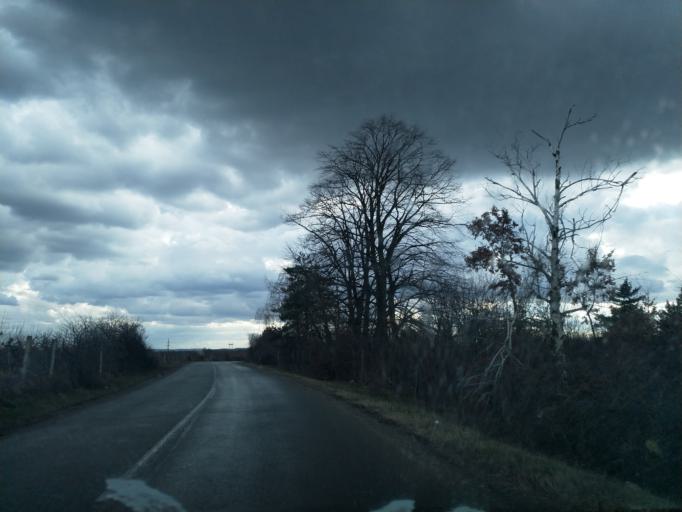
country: RS
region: Central Serbia
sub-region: Belgrade
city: Grocka
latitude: 44.6368
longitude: 20.7502
